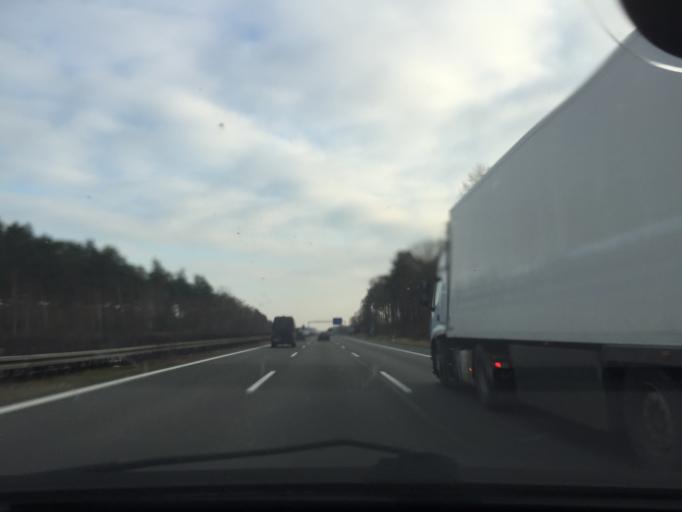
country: DE
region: Brandenburg
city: Fichtenwalde
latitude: 52.3124
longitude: 12.8716
